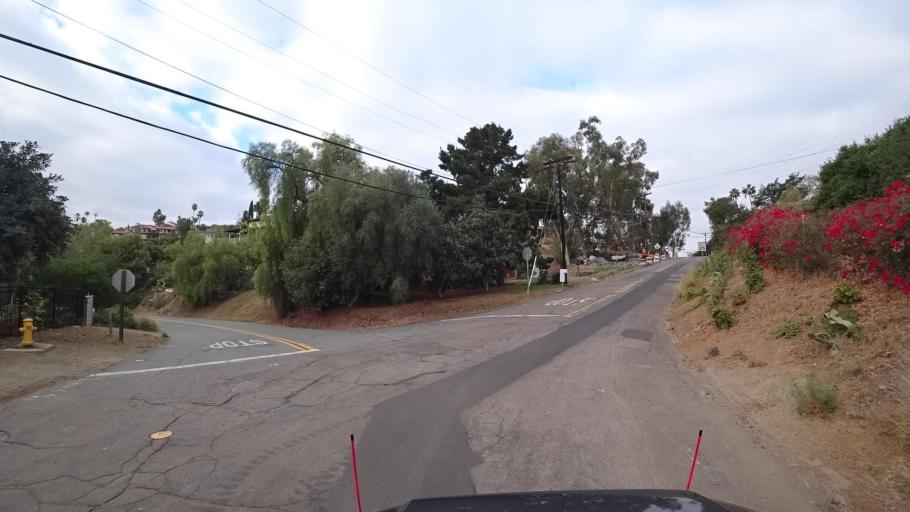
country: US
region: California
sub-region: San Diego County
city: Spring Valley
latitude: 32.7475
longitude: -117.0076
